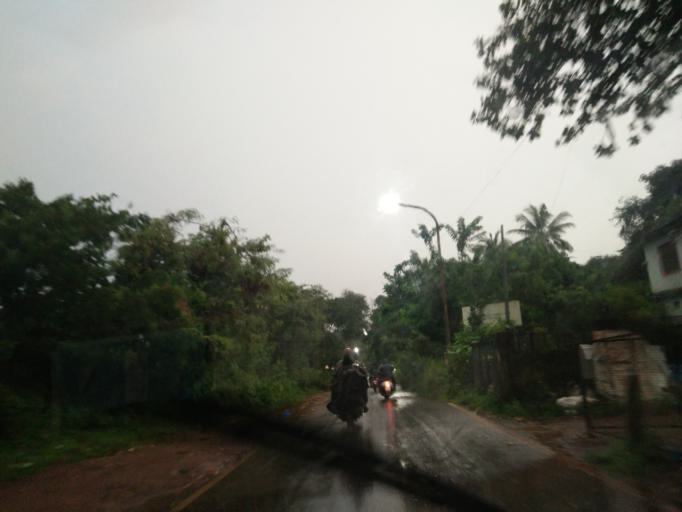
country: IN
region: Goa
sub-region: South Goa
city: Madgaon
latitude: 15.2849
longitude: 73.9648
